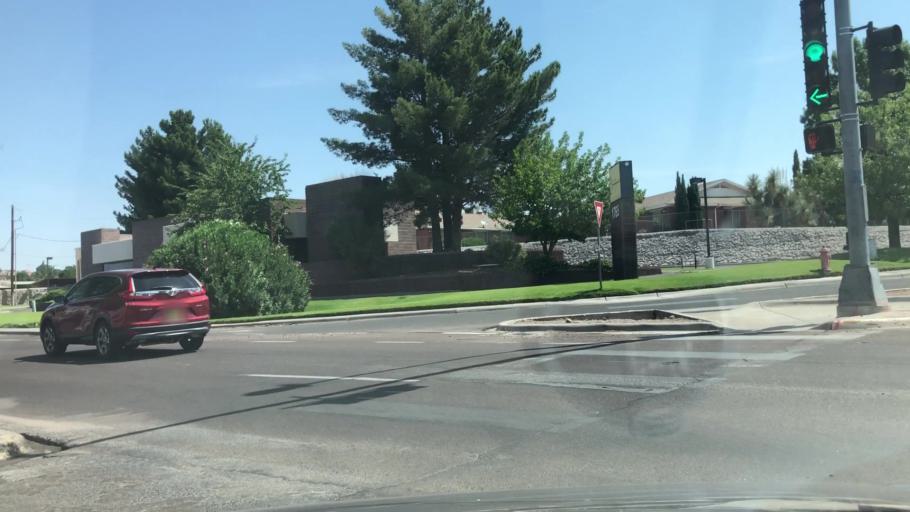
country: US
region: New Mexico
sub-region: Dona Ana County
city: University Park
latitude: 32.3000
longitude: -106.7367
